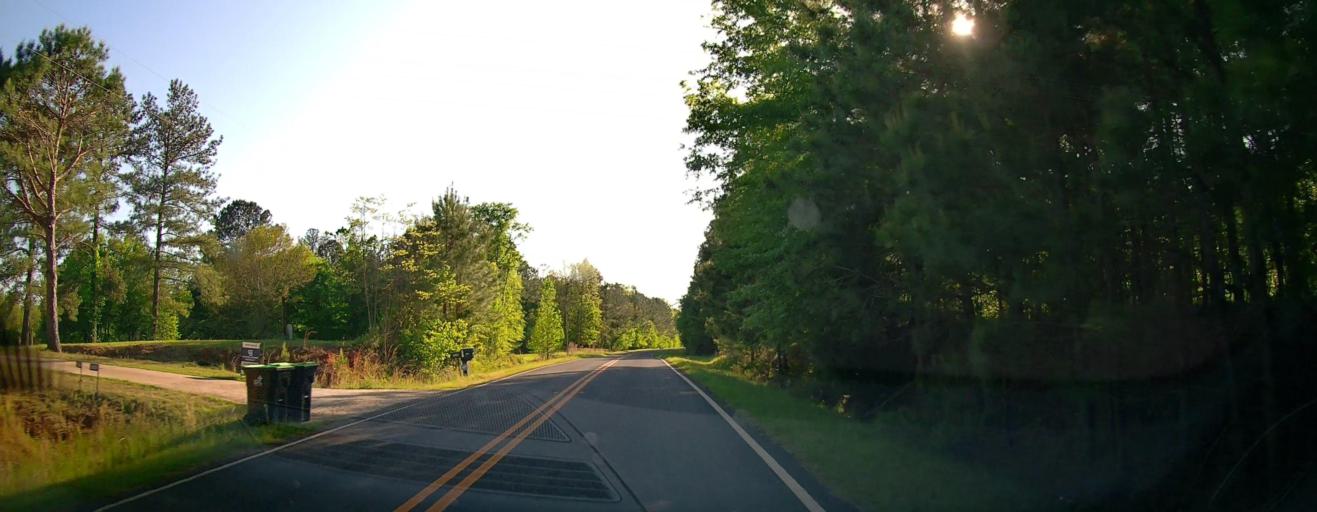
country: US
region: Georgia
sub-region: Macon County
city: Marshallville
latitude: 32.3864
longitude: -83.8551
